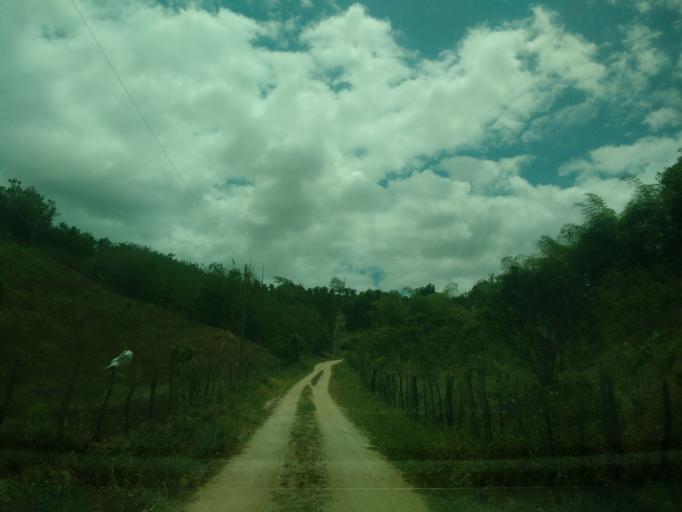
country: BR
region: Alagoas
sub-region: Santana Do Mundau
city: Santana do Mundau
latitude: -9.1542
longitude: -36.1687
